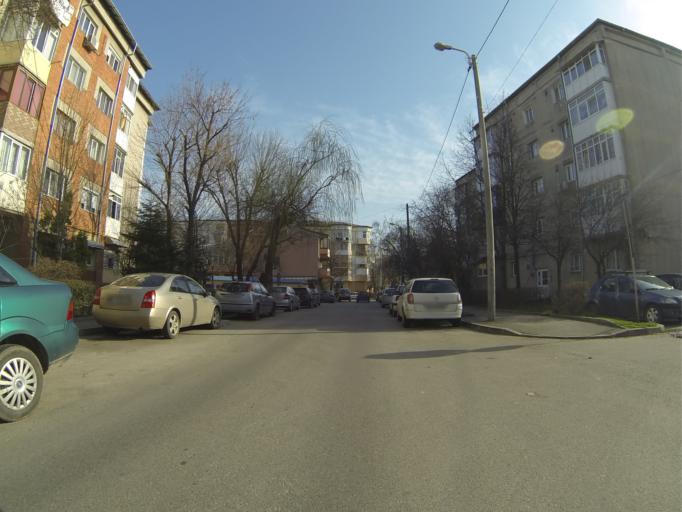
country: RO
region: Dolj
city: Craiova
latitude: 44.3064
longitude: 23.8145
